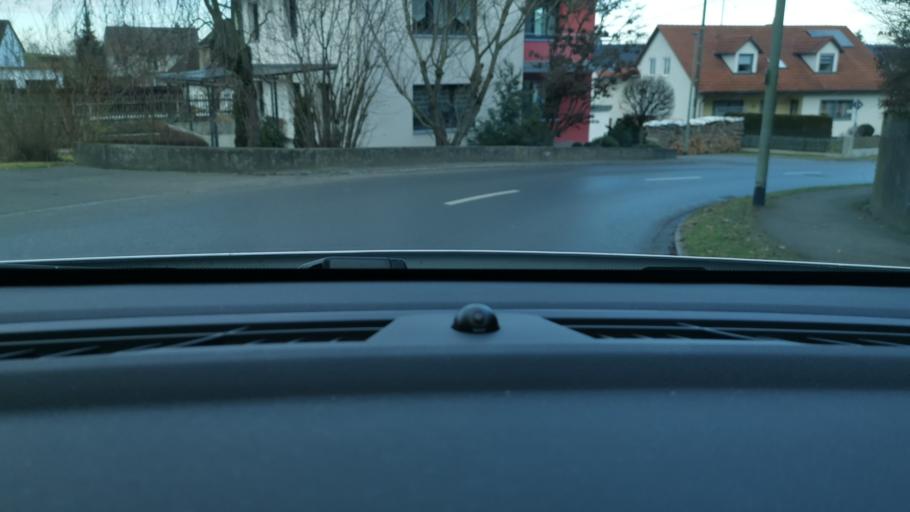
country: DE
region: Bavaria
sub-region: Swabia
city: Affing
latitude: 48.4937
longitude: 10.9813
